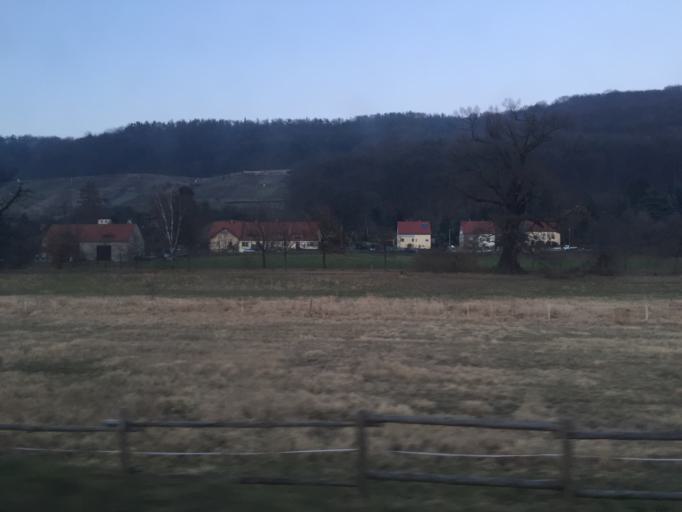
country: DE
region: Saxony
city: Heidenau
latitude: 51.0056
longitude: 13.8840
